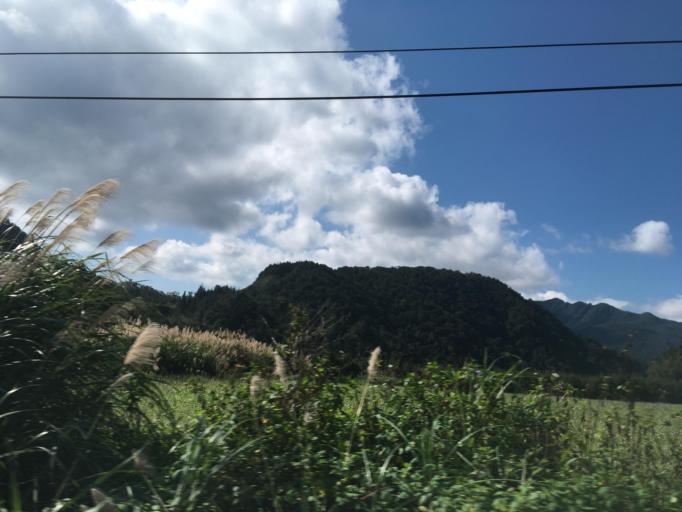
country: TW
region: Taiwan
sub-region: Yilan
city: Yilan
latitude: 24.7520
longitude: 121.6337
